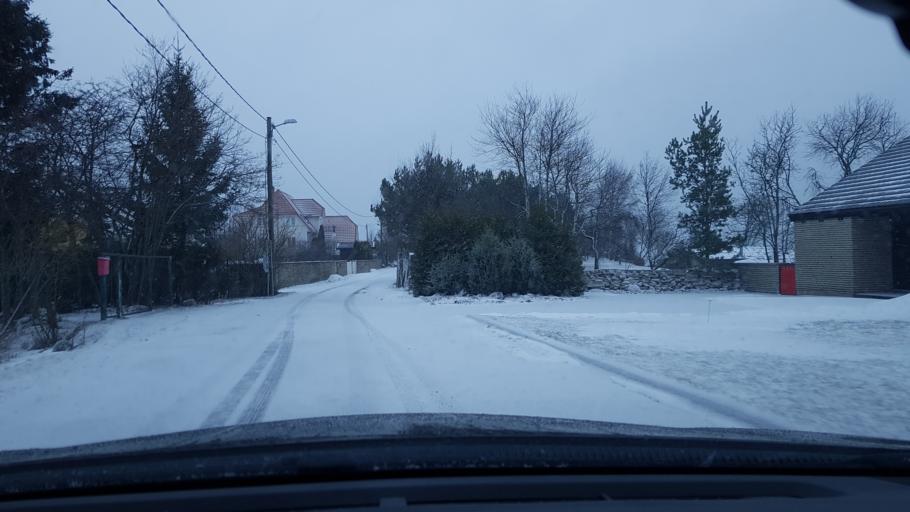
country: EE
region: Harju
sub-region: Raasiku vald
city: Raasiku
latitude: 59.5225
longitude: 25.2749
